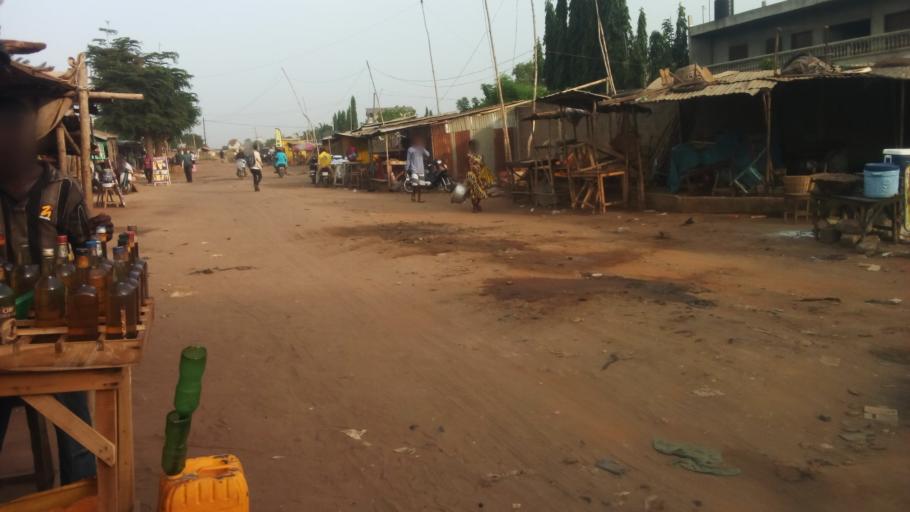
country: BJ
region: Atlantique
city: Abomey-Calavi
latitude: 6.4230
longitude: 2.3386
